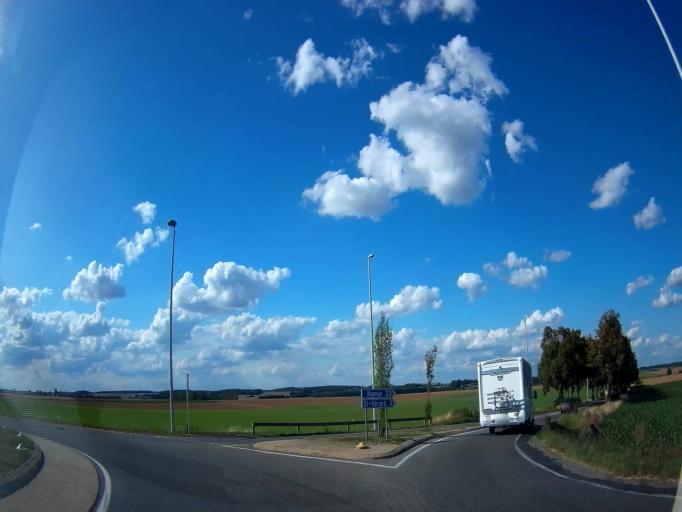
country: BE
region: Wallonia
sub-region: Province de Namur
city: Mettet
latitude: 50.3221
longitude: 4.7405
